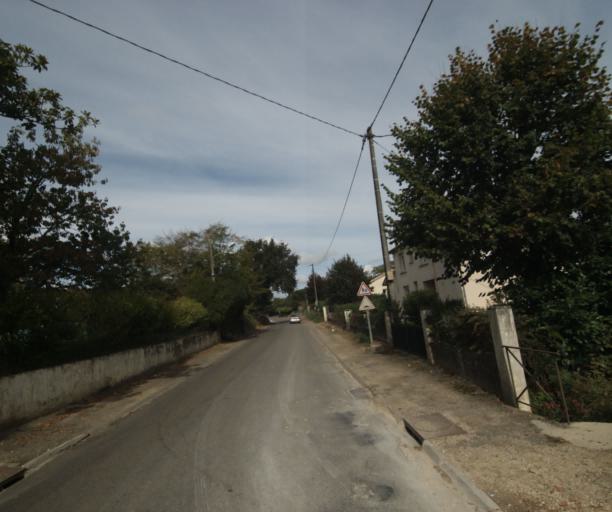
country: FR
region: Midi-Pyrenees
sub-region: Departement du Gers
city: Eauze
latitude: 43.8550
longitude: 0.1029
